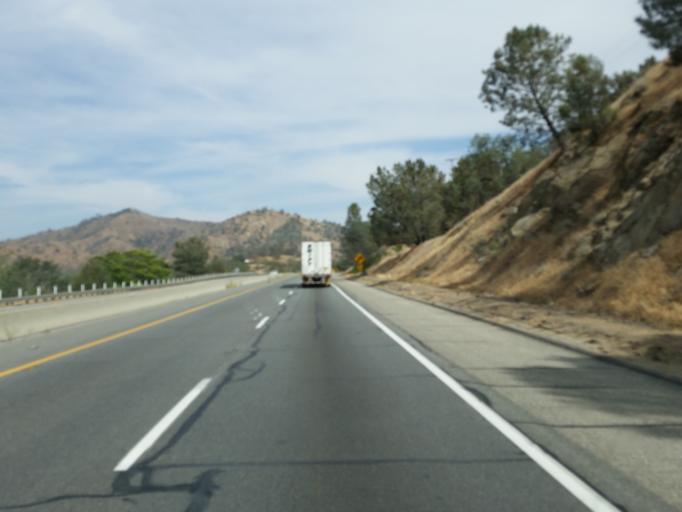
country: US
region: California
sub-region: Kern County
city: Bear Valley Springs
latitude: 35.2323
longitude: -118.5725
